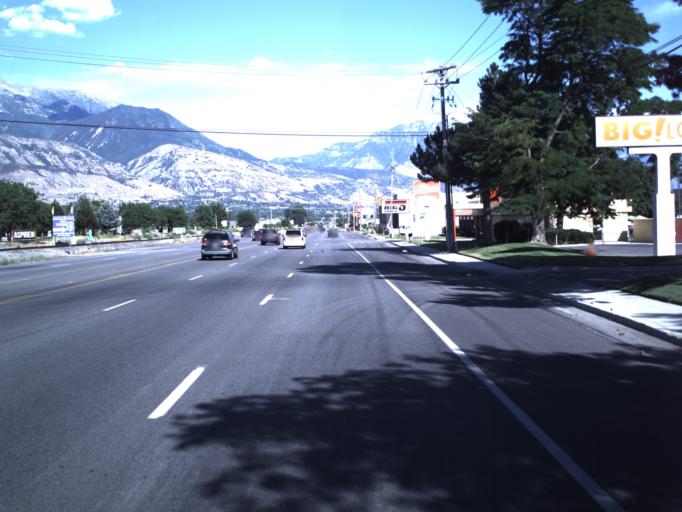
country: US
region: Utah
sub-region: Utah County
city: American Fork
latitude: 40.3725
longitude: -111.7800
